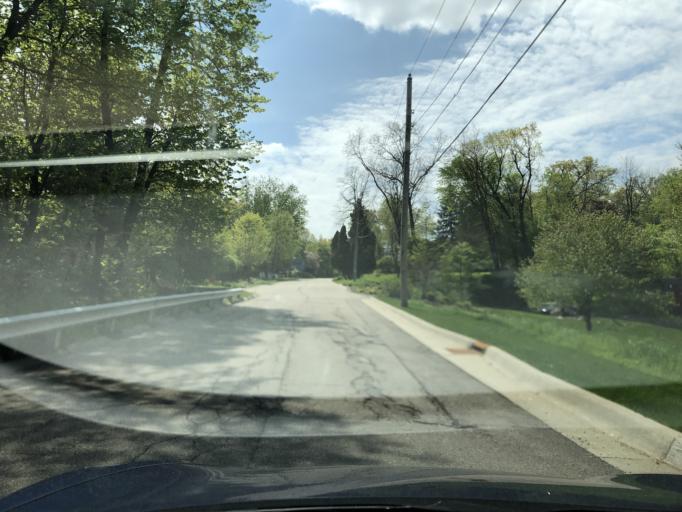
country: US
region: Iowa
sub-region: Dubuque County
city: Dubuque
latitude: 42.4820
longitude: -90.6617
